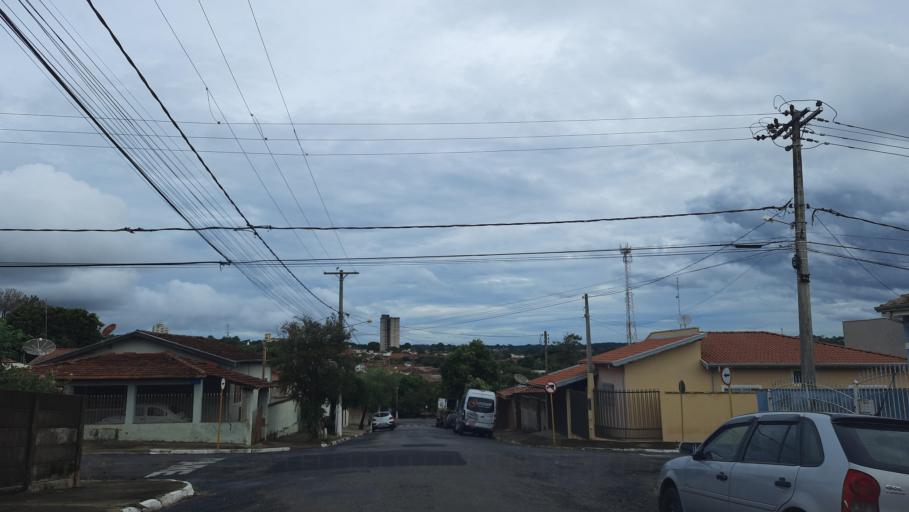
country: BR
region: Sao Paulo
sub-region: Casa Branca
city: Casa Branca
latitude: -21.7663
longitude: -47.0913
